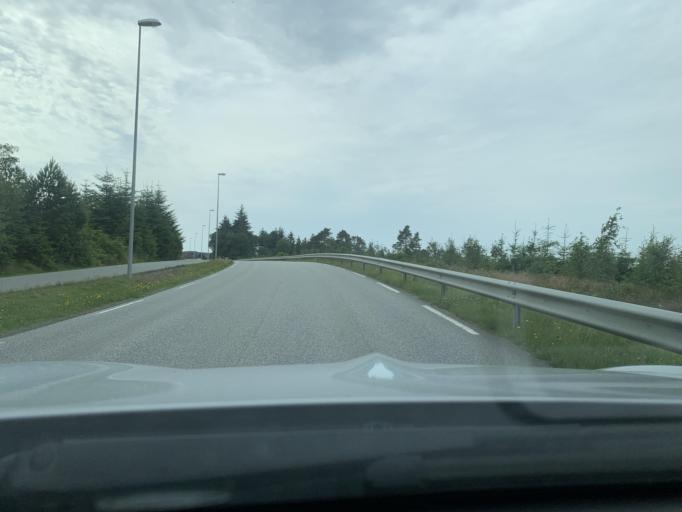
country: NO
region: Rogaland
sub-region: Time
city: Bryne
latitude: 58.7503
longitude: 5.6946
